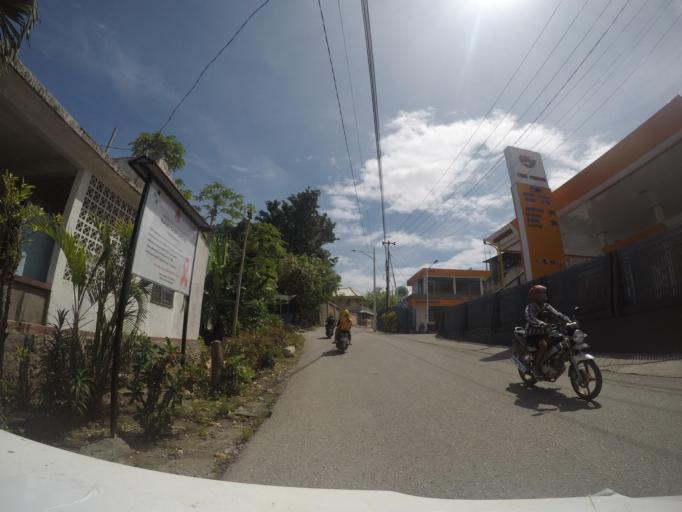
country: TL
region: Baucau
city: Baucau
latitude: -8.4627
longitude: 126.4571
